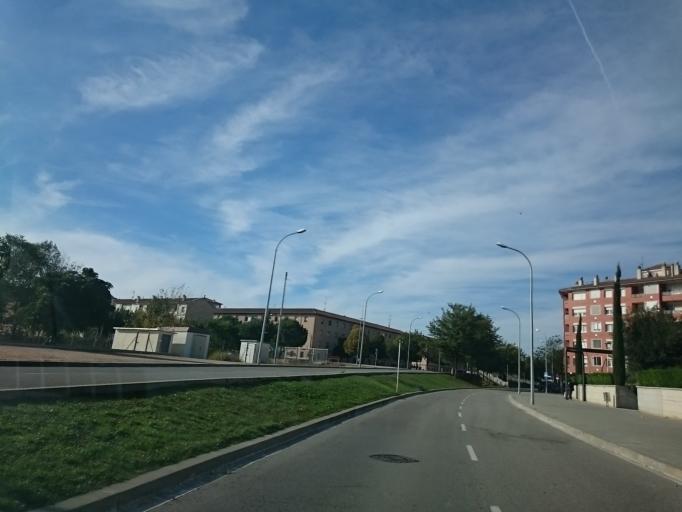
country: ES
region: Catalonia
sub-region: Provincia de Barcelona
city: Vic
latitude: 41.9192
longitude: 2.2501
